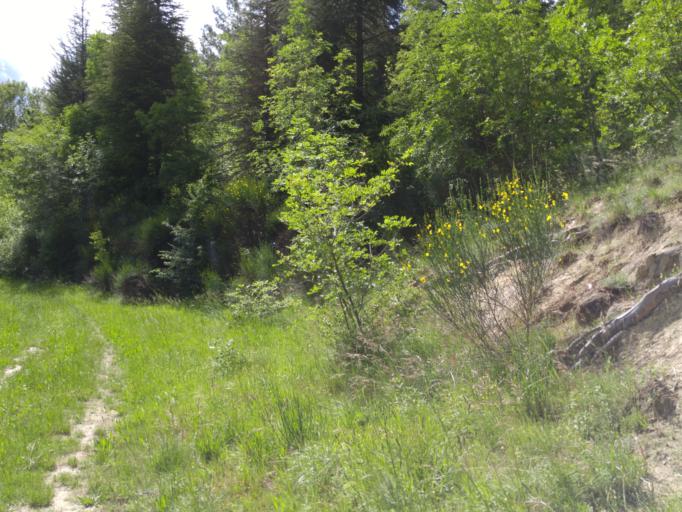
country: IT
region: The Marches
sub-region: Provincia di Pesaro e Urbino
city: Fermignano
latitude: 43.6974
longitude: 12.6250
